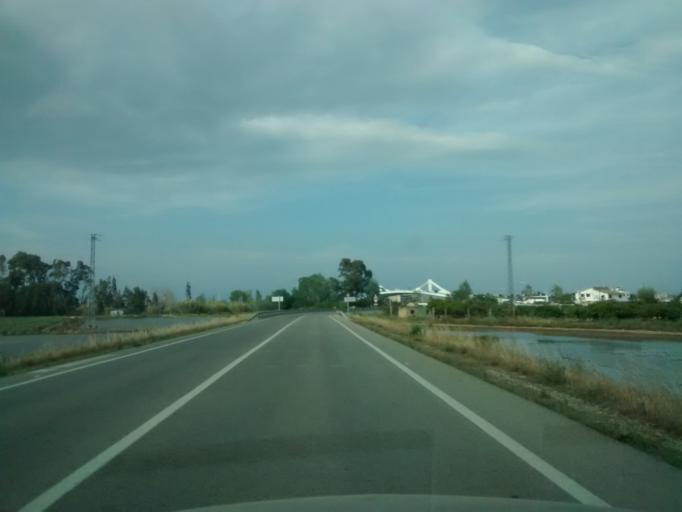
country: ES
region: Catalonia
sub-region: Provincia de Tarragona
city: Deltebre
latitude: 40.7096
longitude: 0.7142
